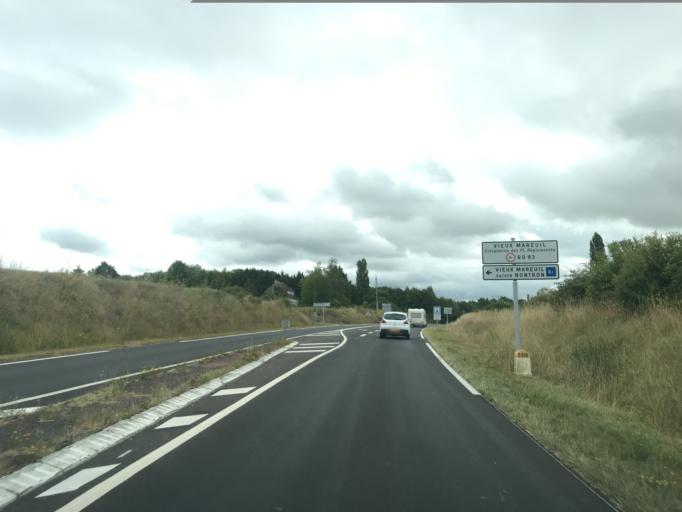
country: FR
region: Aquitaine
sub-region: Departement de la Dordogne
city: Mareuil
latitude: 45.4544
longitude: 0.4539
